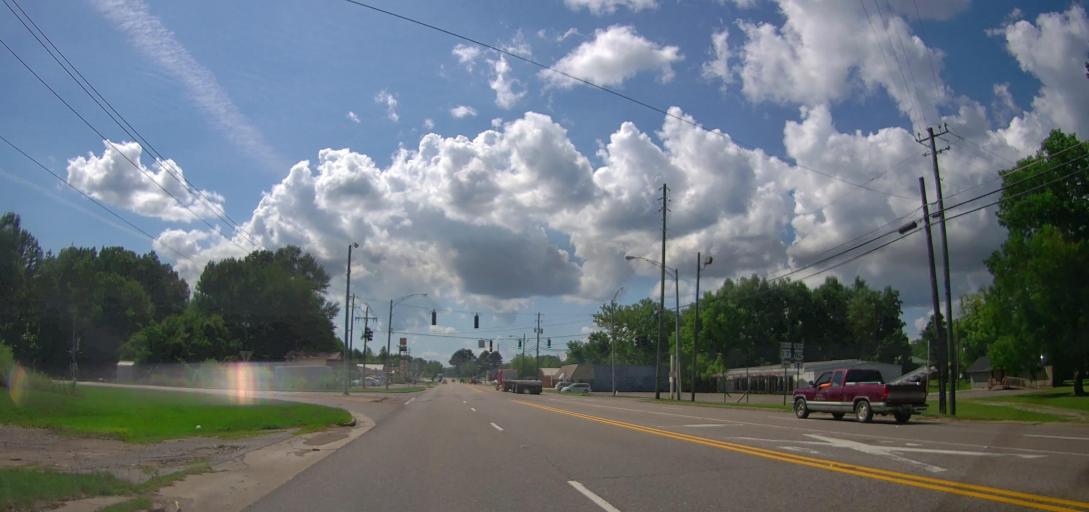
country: US
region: Alabama
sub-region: Pickens County
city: Reform
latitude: 33.3792
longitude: -88.0168
